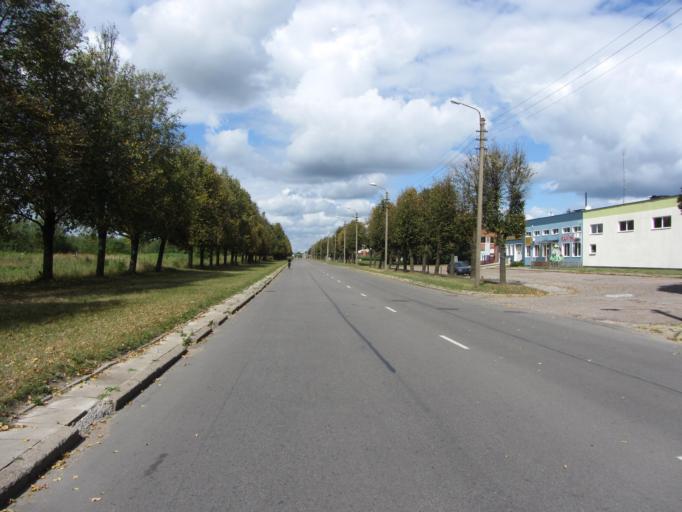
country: LT
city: Baltoji Voke
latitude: 54.6210
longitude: 25.1434
